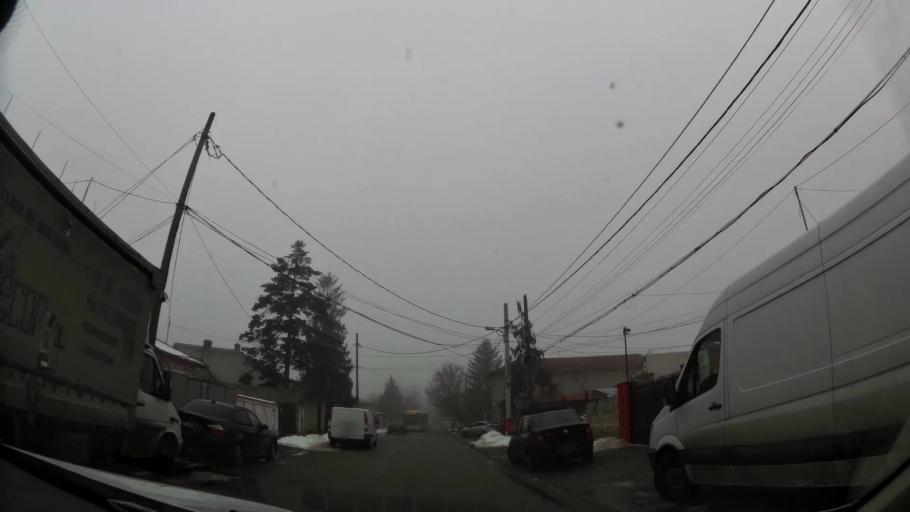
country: RO
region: Ilfov
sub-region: Comuna Chiajna
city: Rosu
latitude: 44.4733
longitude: 26.0039
